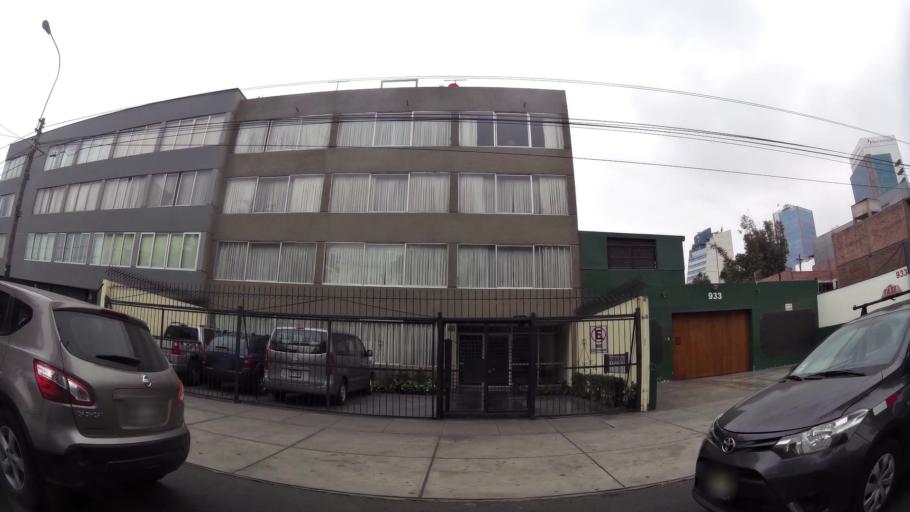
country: PE
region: Lima
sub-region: Lima
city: San Isidro
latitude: -12.1021
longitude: -77.0207
